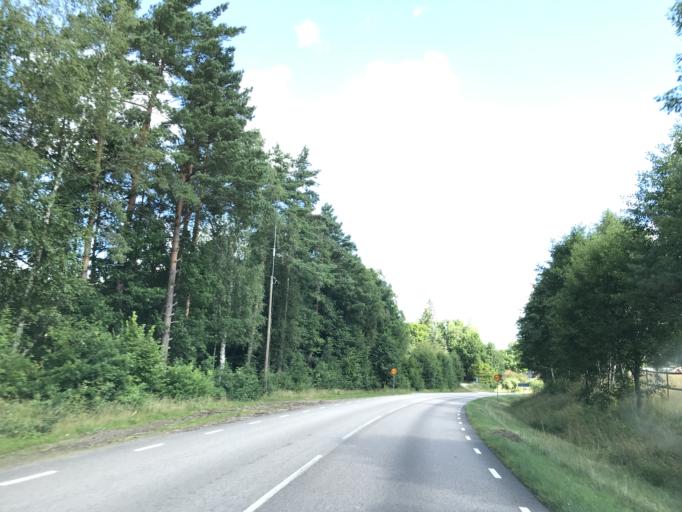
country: SE
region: Halland
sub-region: Laholms Kommun
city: Knared
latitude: 56.5087
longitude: 13.3196
